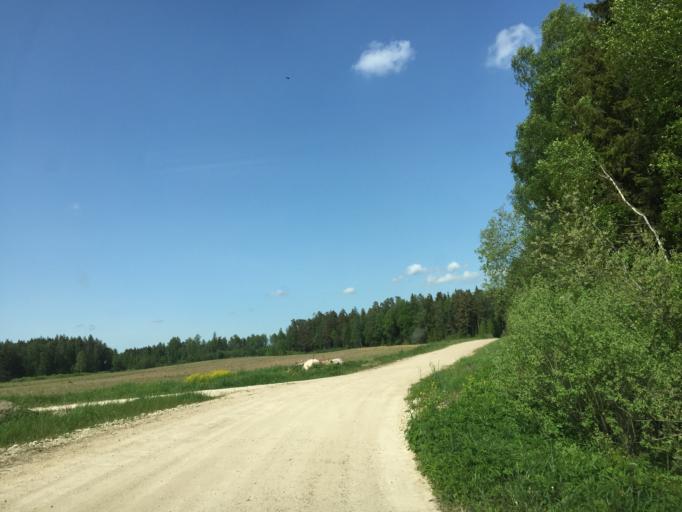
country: LV
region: Baldone
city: Baldone
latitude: 56.7957
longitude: 24.4203
